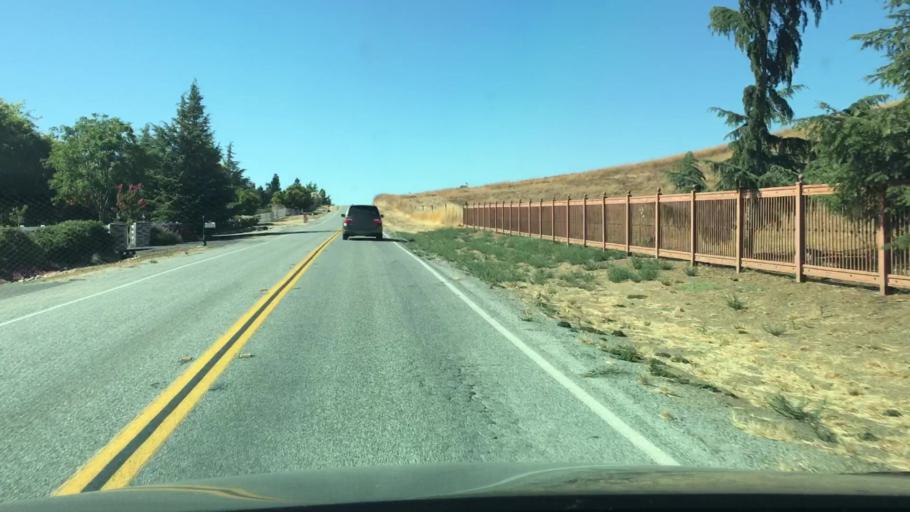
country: US
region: California
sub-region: Santa Clara County
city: San Martin
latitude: 37.0900
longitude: -121.5685
